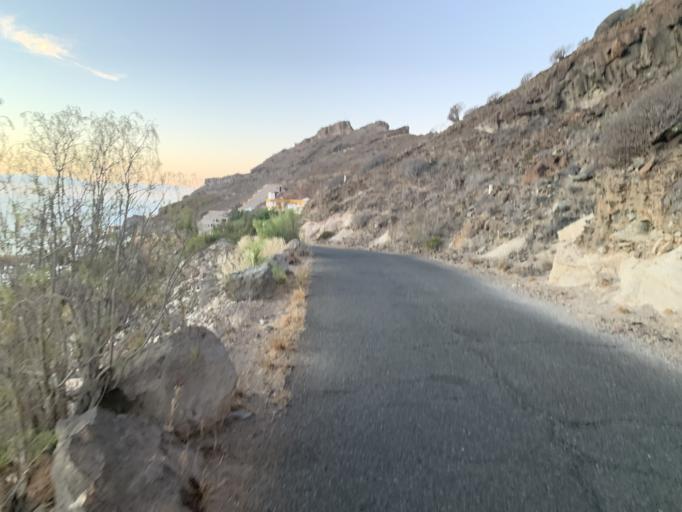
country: ES
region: Canary Islands
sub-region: Provincia de Las Palmas
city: Puerto Rico
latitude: 27.8055
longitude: -15.7327
